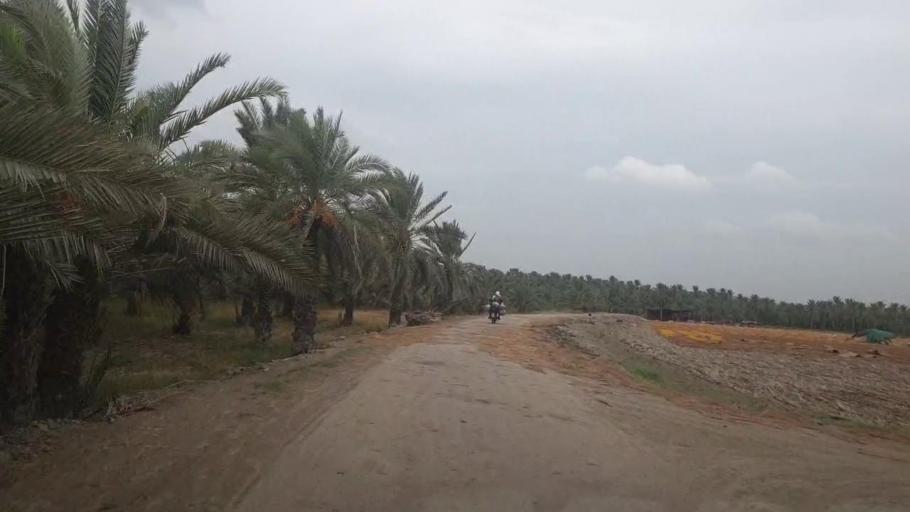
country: PK
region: Sindh
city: Khairpur
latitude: 27.5725
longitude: 68.7389
